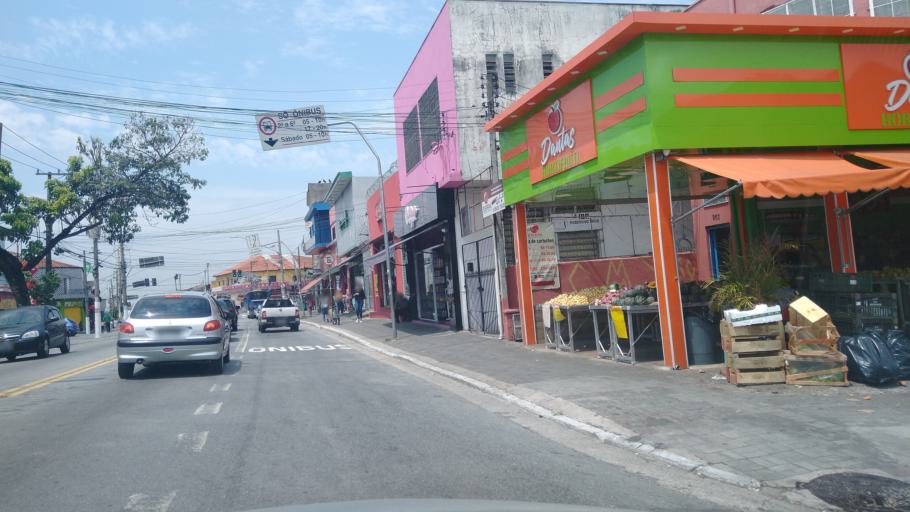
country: BR
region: Sao Paulo
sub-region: Sao Paulo
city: Sao Paulo
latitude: -23.4689
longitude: -46.6772
